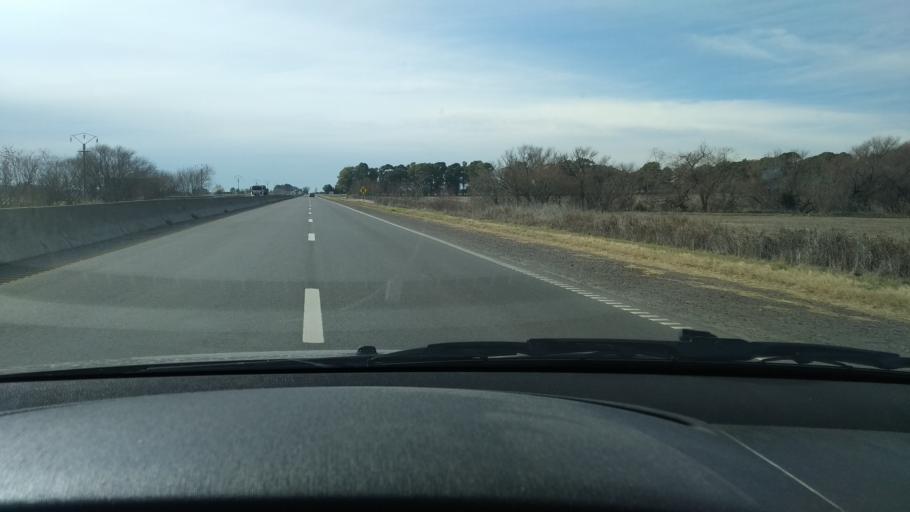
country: AR
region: Buenos Aires
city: Olavarria
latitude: -36.9120
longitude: -60.1989
